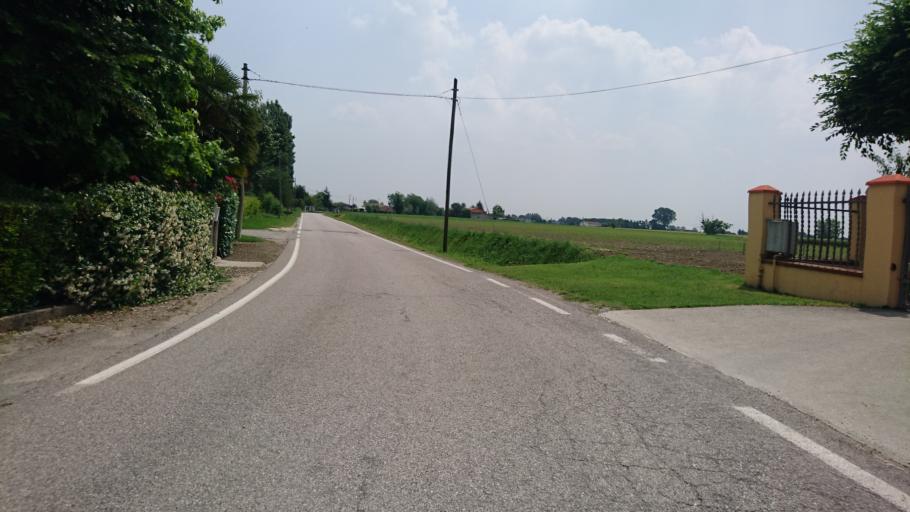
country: IT
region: Veneto
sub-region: Provincia di Padova
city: Cartura
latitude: 45.2625
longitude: 11.8810
